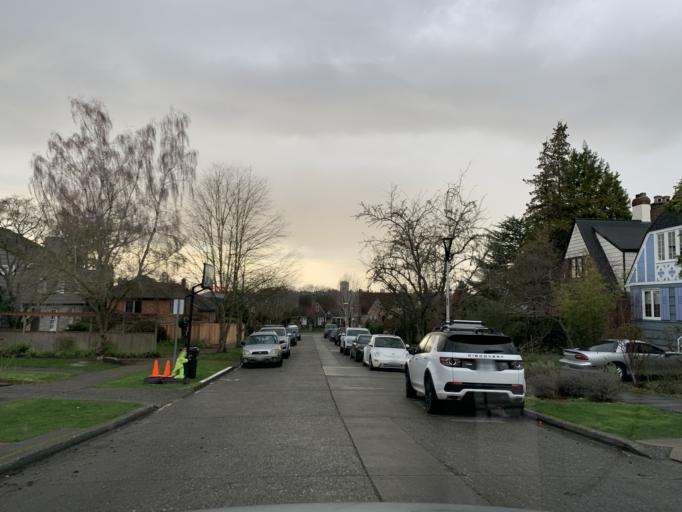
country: US
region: Washington
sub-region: King County
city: Yarrow Point
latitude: 47.6591
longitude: -122.2801
